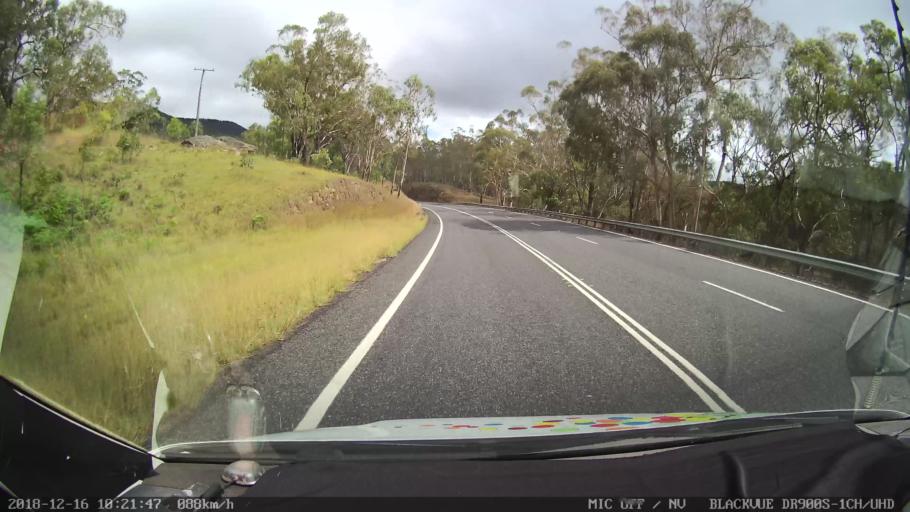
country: AU
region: New South Wales
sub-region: Tenterfield Municipality
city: Carrolls Creek
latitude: -29.2025
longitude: 152.0140
